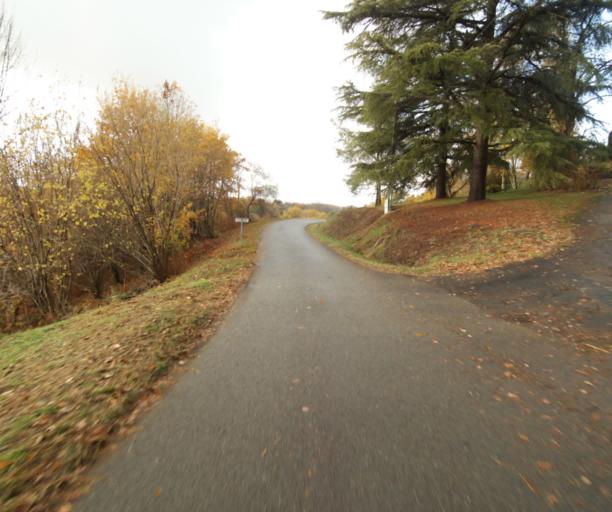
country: FR
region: Limousin
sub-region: Departement de la Correze
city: Cornil
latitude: 45.2224
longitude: 1.6584
